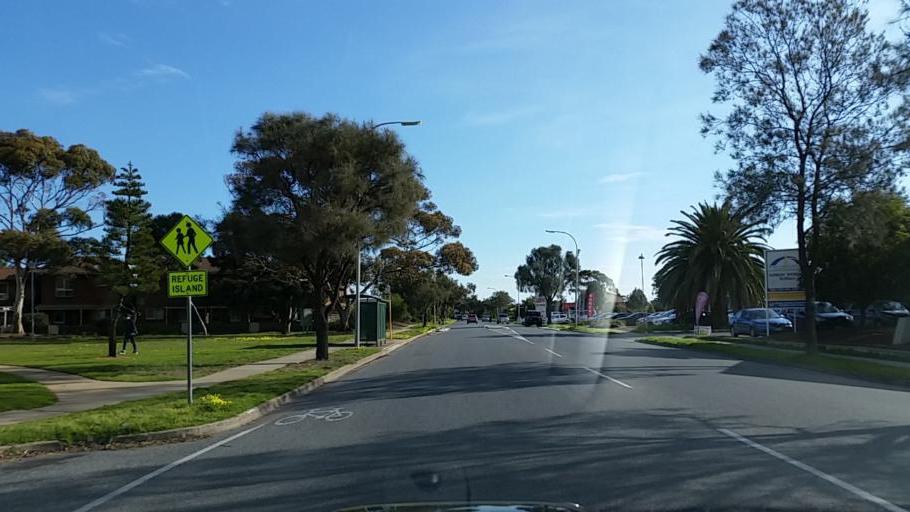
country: AU
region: South Australia
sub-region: Charles Sturt
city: West Lakes Shore
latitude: -34.8603
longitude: 138.4905
